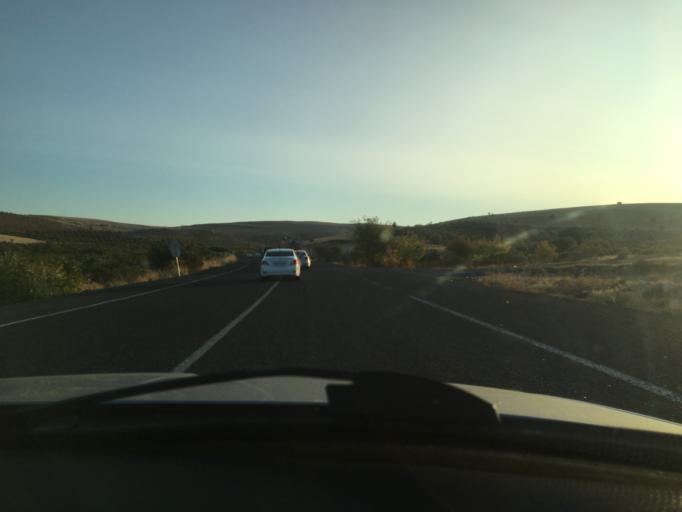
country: TR
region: Sanliurfa
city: Halfeti
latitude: 37.1990
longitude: 37.9675
